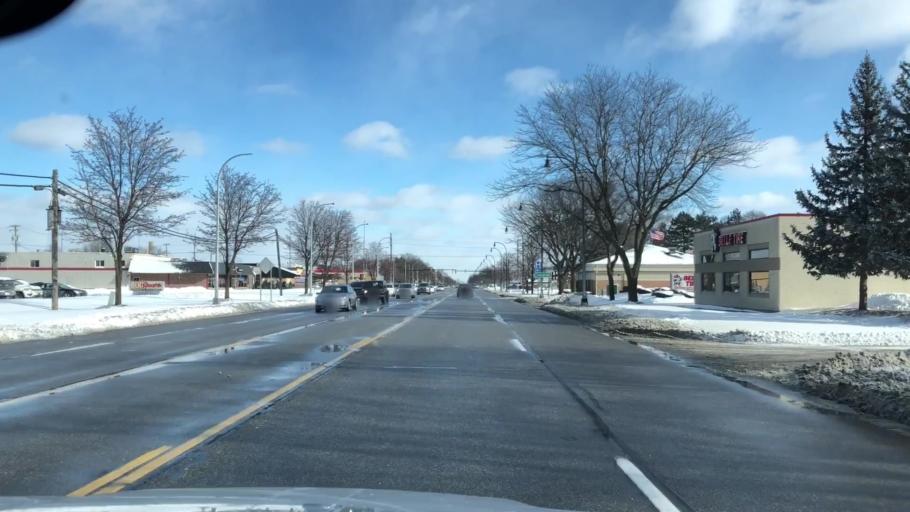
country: US
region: Michigan
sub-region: Wayne County
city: Westland
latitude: 42.3676
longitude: -83.4048
